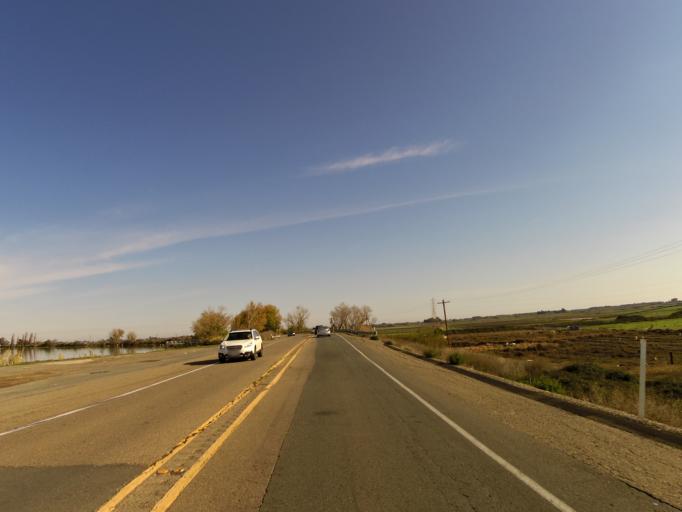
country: US
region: California
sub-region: Solano County
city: Rio Vista
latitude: 38.0825
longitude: -121.7137
